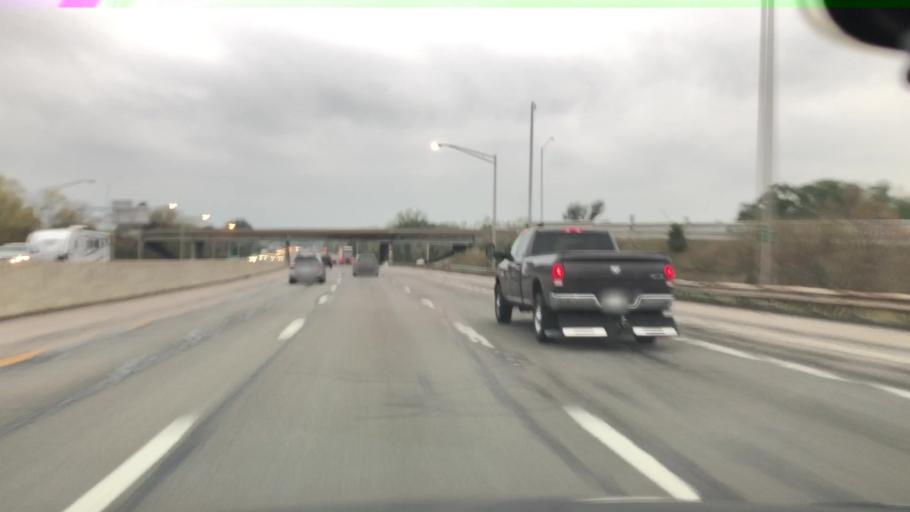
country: US
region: Ohio
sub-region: Lorain County
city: North Ridgeville
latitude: 41.3794
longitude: -81.9923
